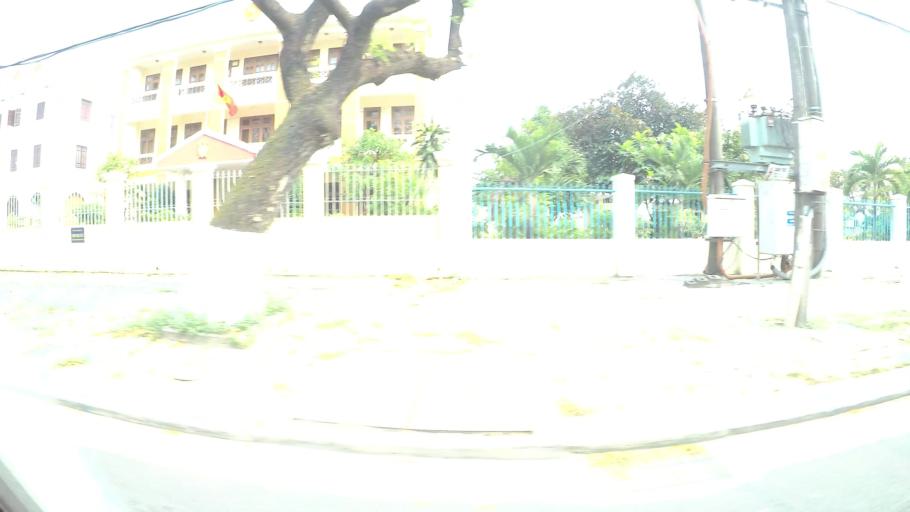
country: VN
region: Da Nang
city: Da Nang
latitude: 16.0473
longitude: 108.2120
